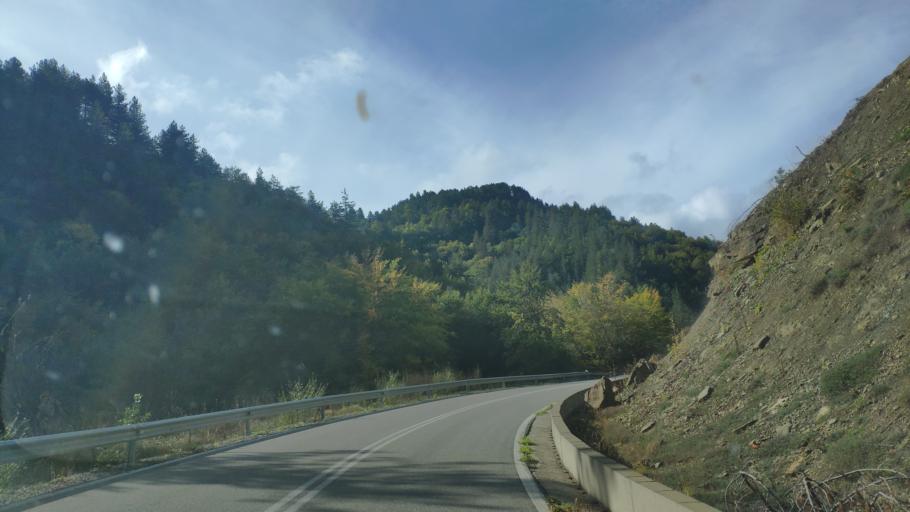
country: GR
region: West Macedonia
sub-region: Nomos Kastorias
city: Nestorio
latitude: 40.3732
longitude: 20.9376
